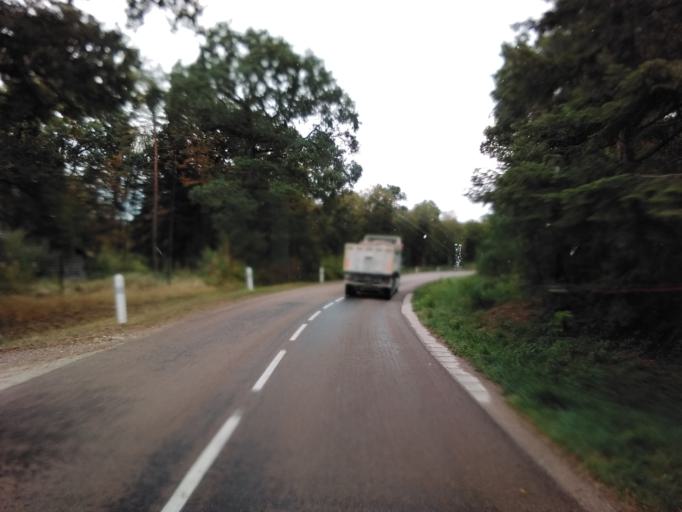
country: FR
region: Champagne-Ardenne
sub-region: Departement de l'Aube
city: Vendeuvre-sur-Barse
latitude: 48.2577
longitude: 4.4909
